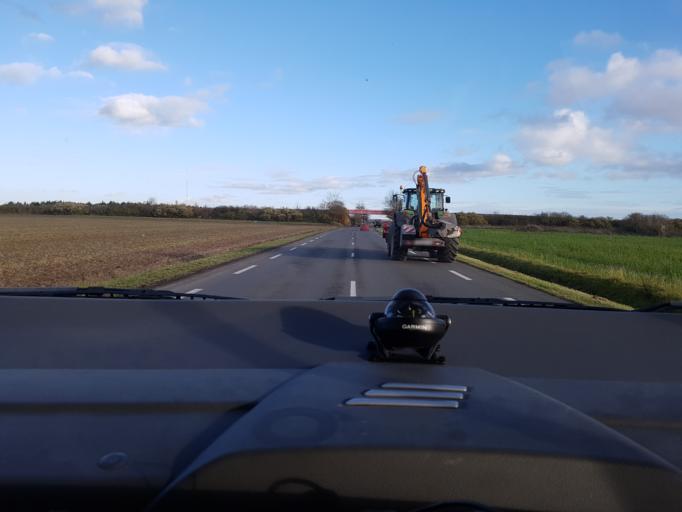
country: FR
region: Nord-Pas-de-Calais
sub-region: Departement du Pas-de-Calais
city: Carvin
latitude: 50.5071
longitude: 2.9585
